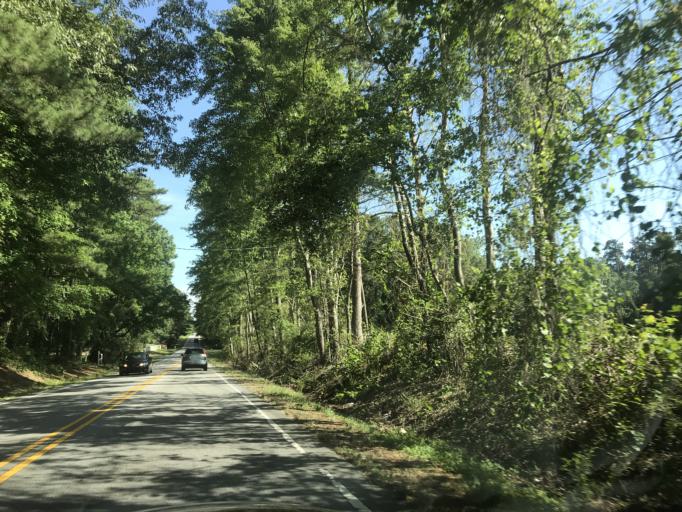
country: US
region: North Carolina
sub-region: Wake County
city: Garner
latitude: 35.6811
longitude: -78.5789
